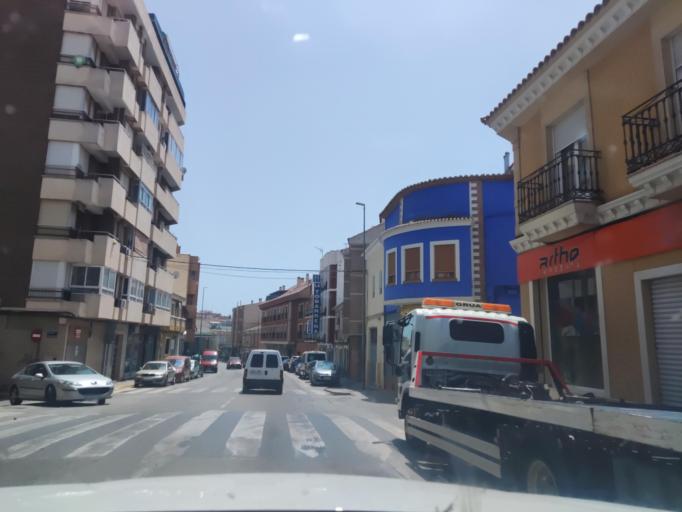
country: ES
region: Castille-La Mancha
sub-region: Provincia de Albacete
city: Hellin
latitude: 38.5131
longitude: -1.6973
